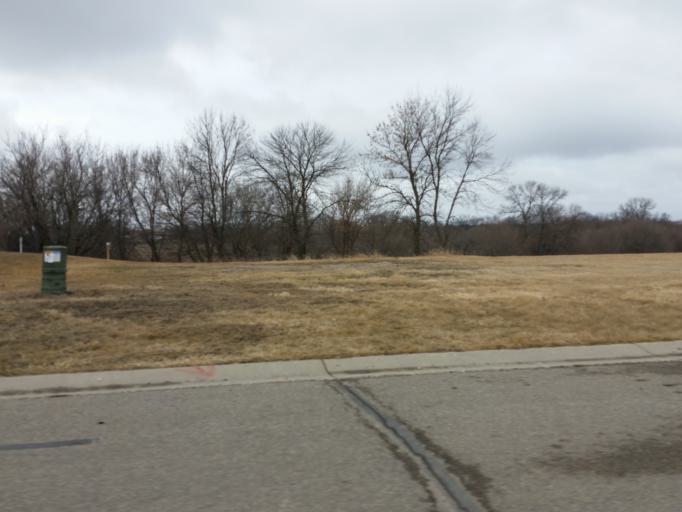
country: US
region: North Dakota
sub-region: Traill County
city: Mayville
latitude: 47.4916
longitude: -97.3122
